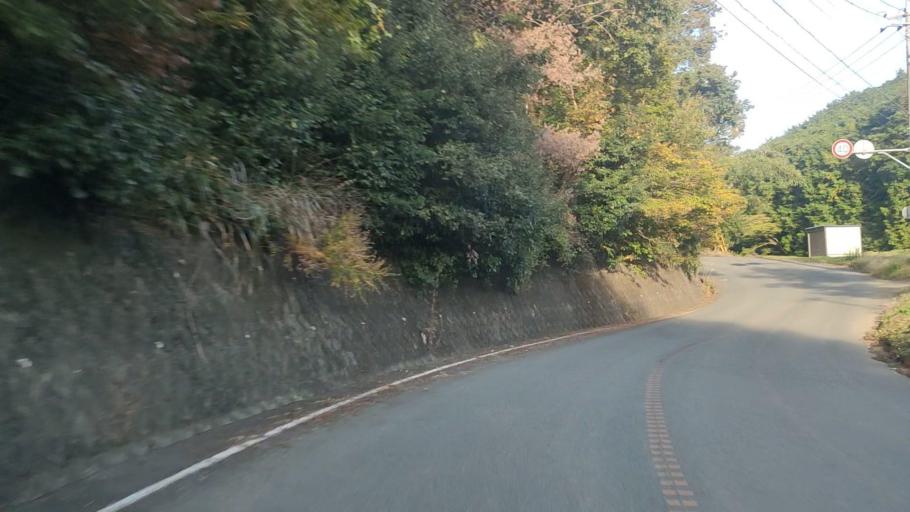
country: JP
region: Shizuoka
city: Mishima
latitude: 35.1532
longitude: 138.9314
